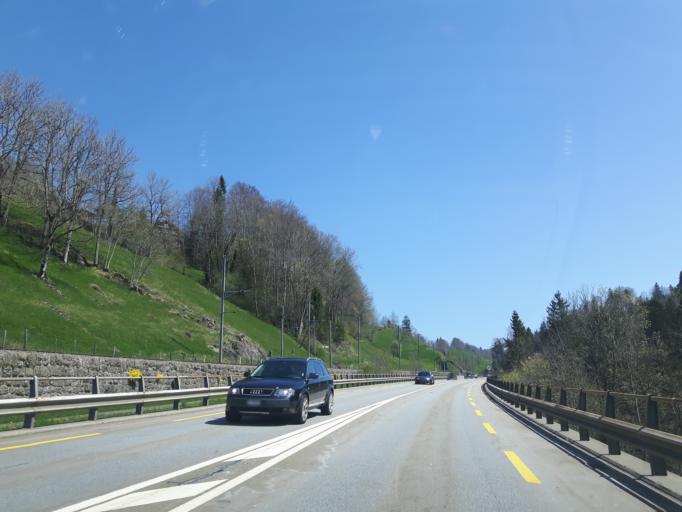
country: CH
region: Schwyz
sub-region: Bezirk Schwyz
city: Sattel
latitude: 47.0848
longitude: 8.6437
